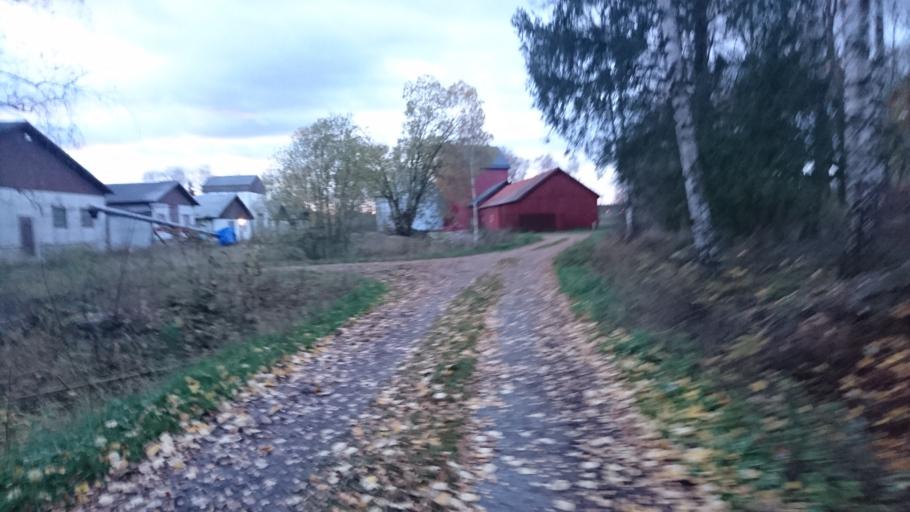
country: SE
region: Vaestmanland
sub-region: Vasteras
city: Tillberga
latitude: 59.7975
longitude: 16.6493
